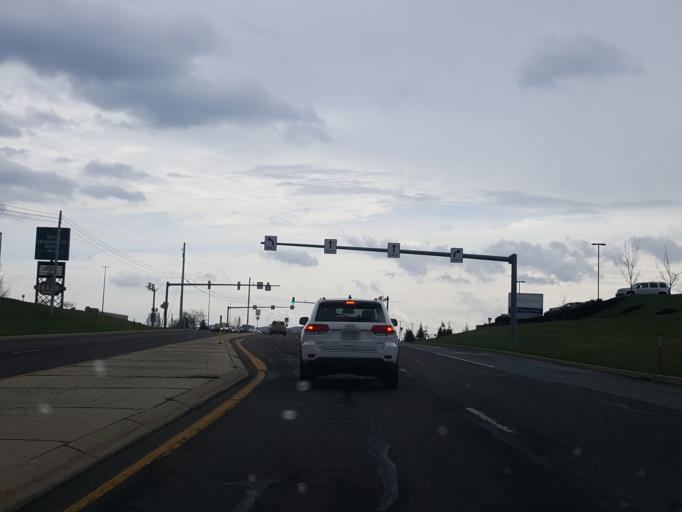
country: US
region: Pennsylvania
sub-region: Berks County
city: Spring Ridge
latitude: 40.3615
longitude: -75.9898
